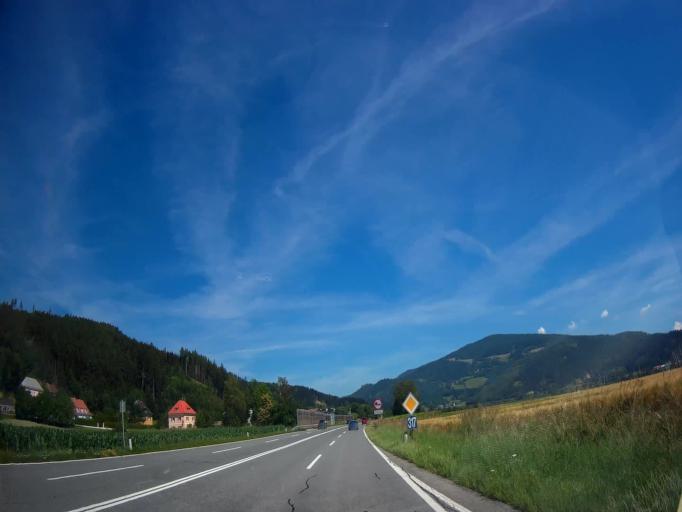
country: AT
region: Carinthia
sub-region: Politischer Bezirk Sankt Veit an der Glan
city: Molbling
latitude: 46.8659
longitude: 14.4491
